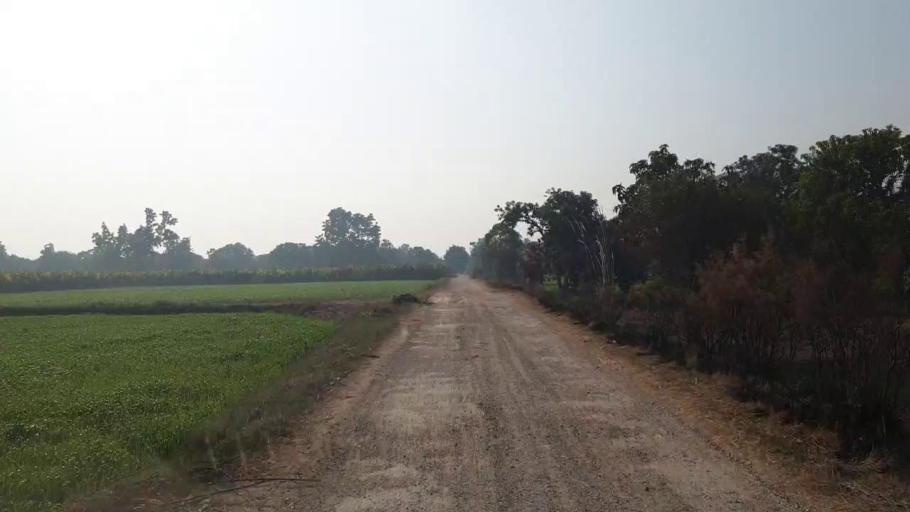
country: PK
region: Sindh
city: Sakrand
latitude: 25.9936
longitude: 68.3674
